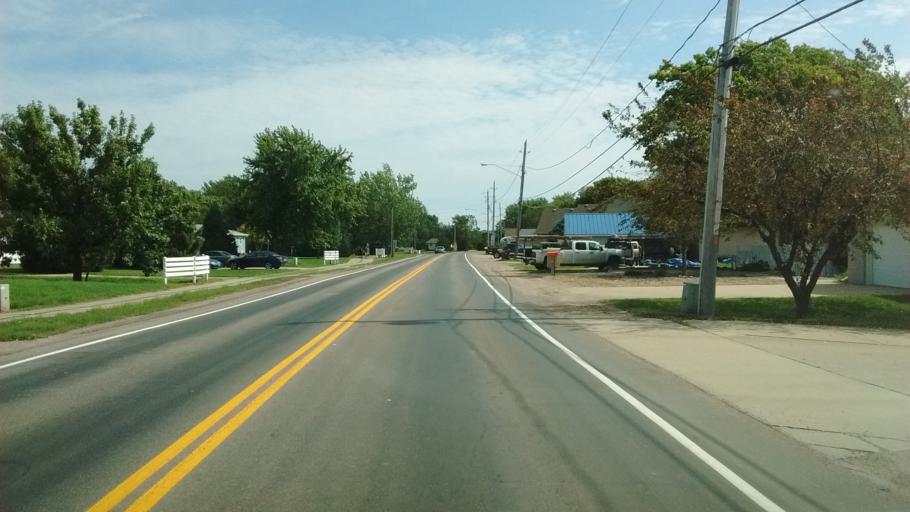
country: US
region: South Dakota
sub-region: Union County
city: North Sioux City
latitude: 42.5503
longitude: -96.5185
